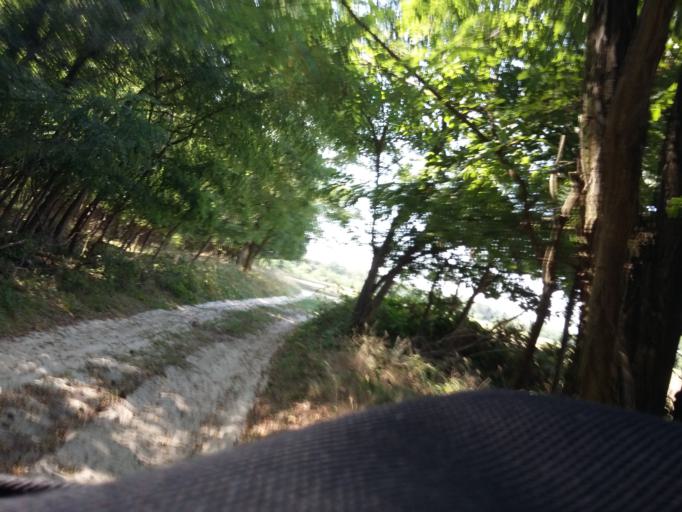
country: SK
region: Bratislavsky
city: Stupava
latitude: 48.3198
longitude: 17.0351
